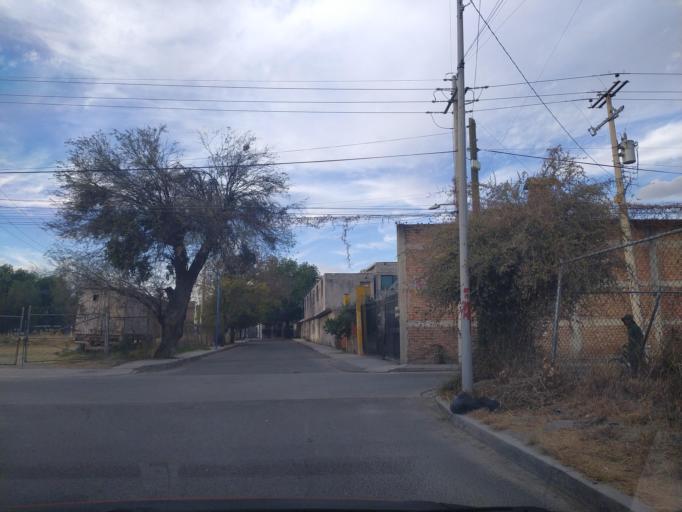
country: LA
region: Oudomxai
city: Muang La
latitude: 21.0330
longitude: 101.8836
